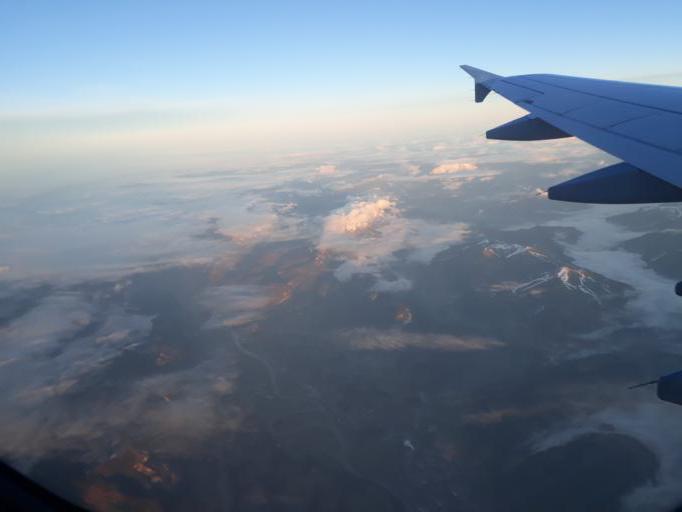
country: AT
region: Tyrol
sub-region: Politischer Bezirk Kufstein
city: Radfeld
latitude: 47.4695
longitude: 11.9403
